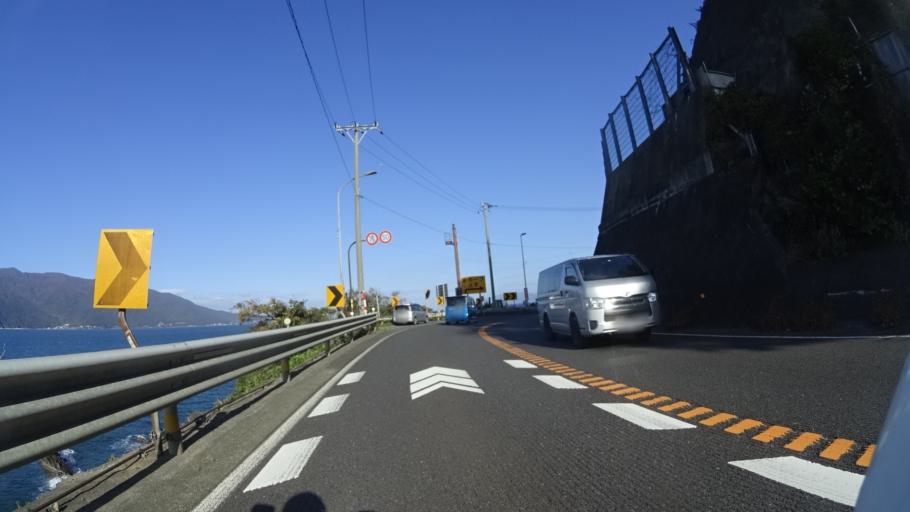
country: JP
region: Fukui
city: Tsuruga
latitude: 35.7030
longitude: 136.0787
